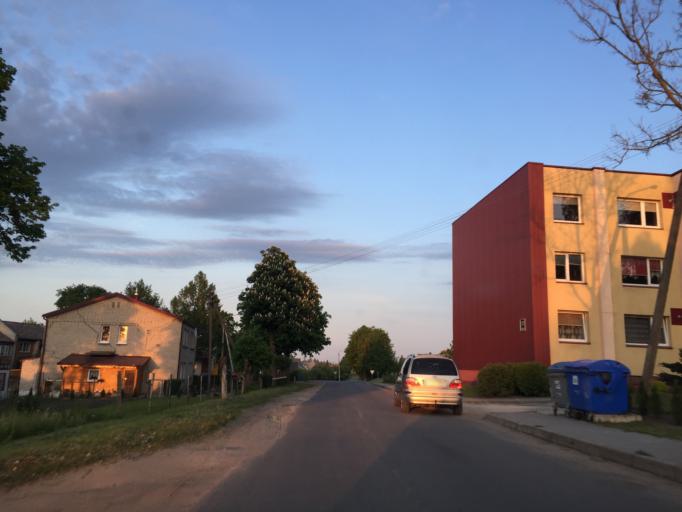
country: LT
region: Siauliu apskritis
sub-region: Siauliai
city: Siauliai
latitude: 55.9845
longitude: 23.1383
